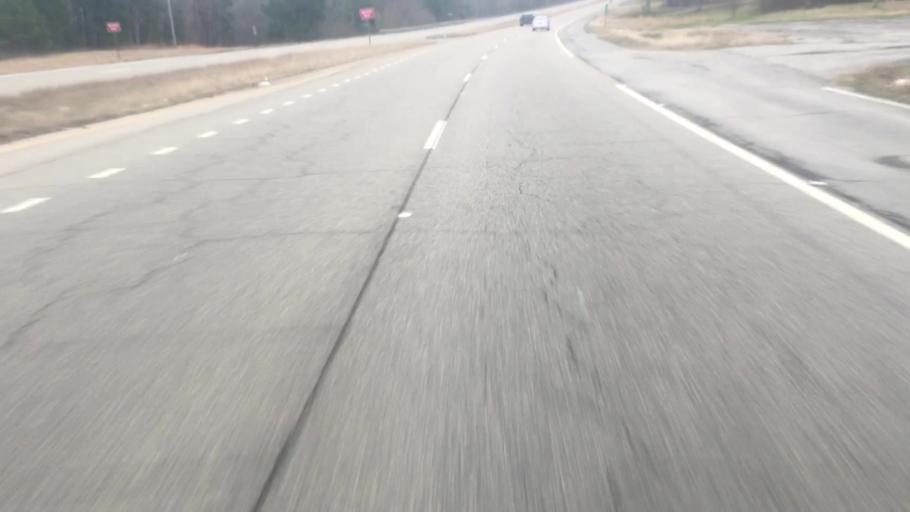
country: US
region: Alabama
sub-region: Walker County
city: Cordova
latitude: 33.8193
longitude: -87.1526
